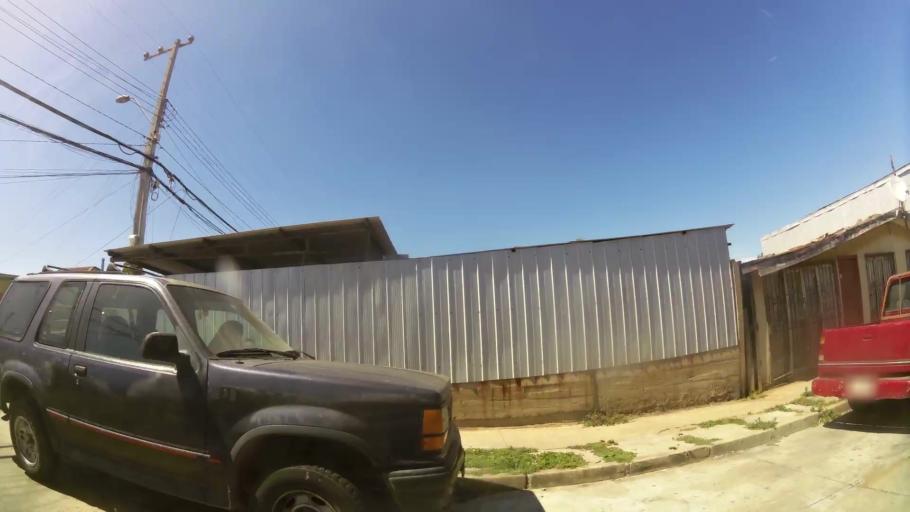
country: CL
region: Valparaiso
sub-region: Provincia de Valparaiso
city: Vina del Mar
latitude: -33.0518
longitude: -71.5818
